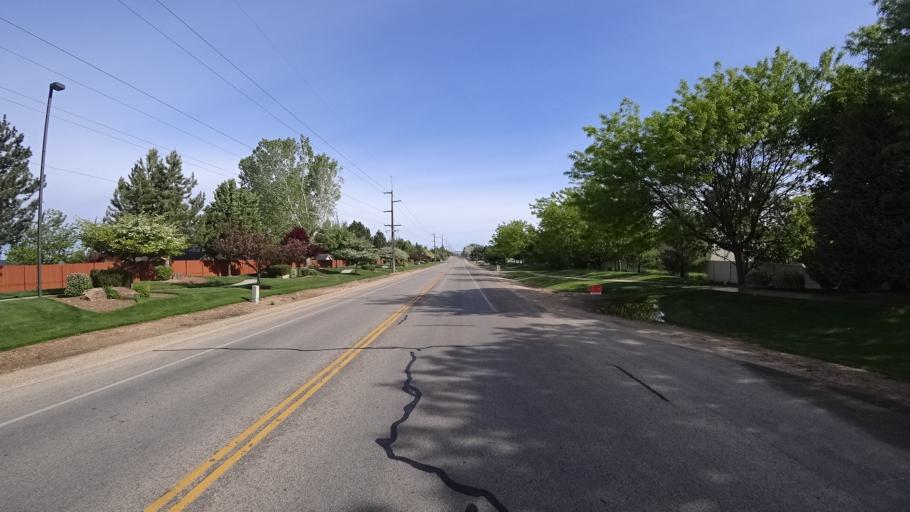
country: US
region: Idaho
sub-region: Ada County
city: Meridian
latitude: 43.5491
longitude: -116.3344
